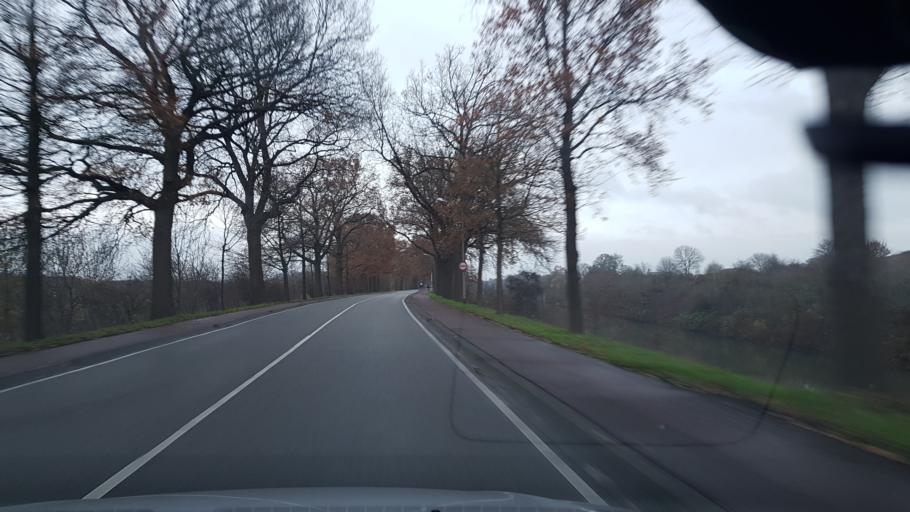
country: NL
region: Limburg
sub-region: Gemeente Maastricht
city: Maastricht
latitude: 50.8744
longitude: 5.6806
